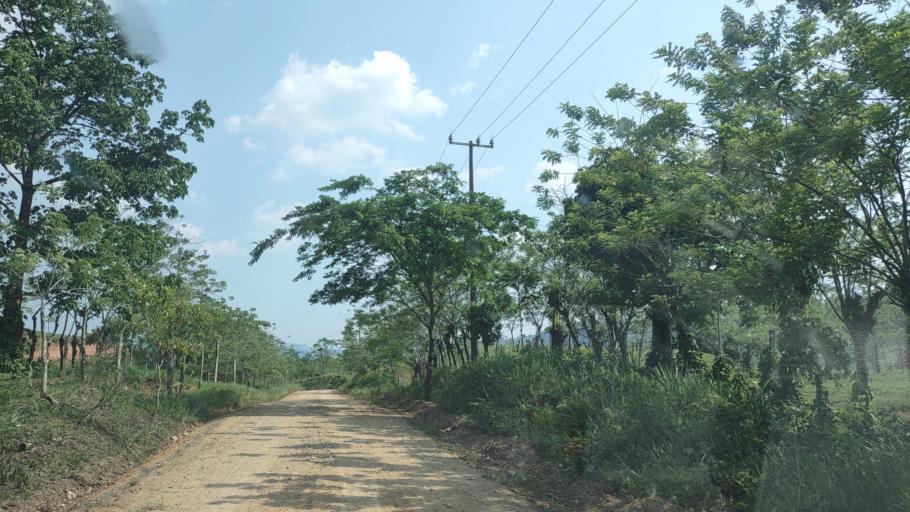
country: MX
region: Chiapas
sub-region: Tecpatan
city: Raudales Malpaso
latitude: 17.3435
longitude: -93.7551
